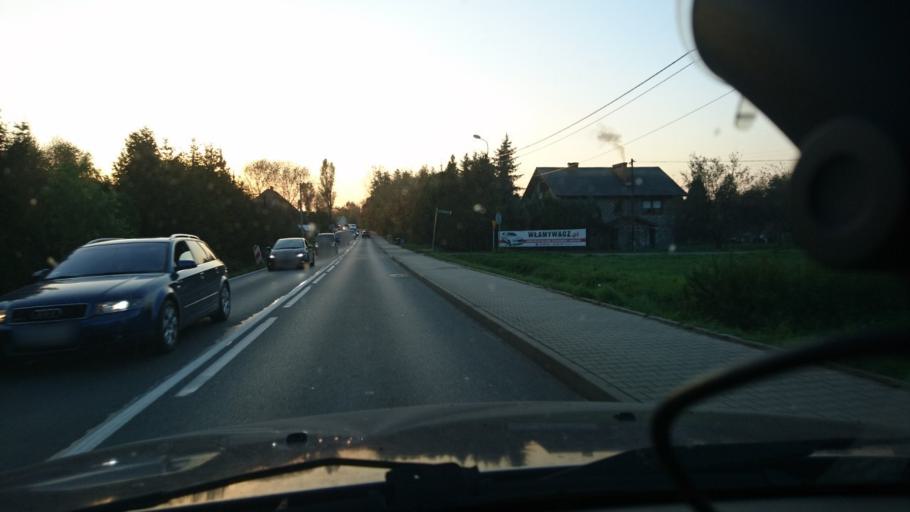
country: PL
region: Silesian Voivodeship
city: Janowice
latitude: 49.8521
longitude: 19.1065
